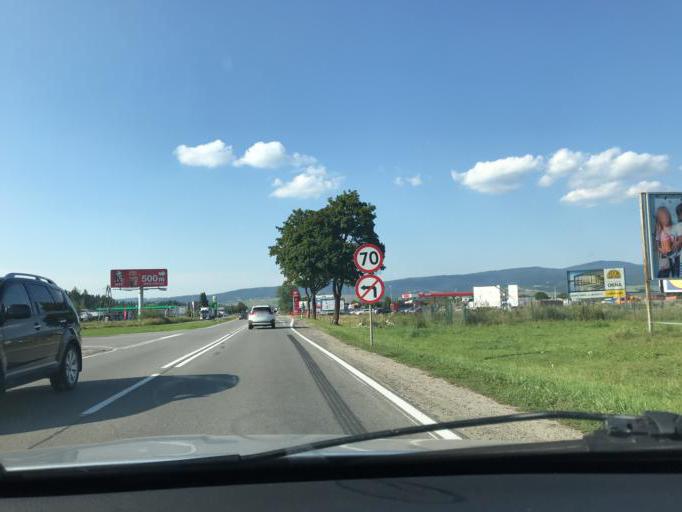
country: PL
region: Lesser Poland Voivodeship
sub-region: Powiat nowotarski
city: Szaflary
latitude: 49.4513
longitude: 20.0204
